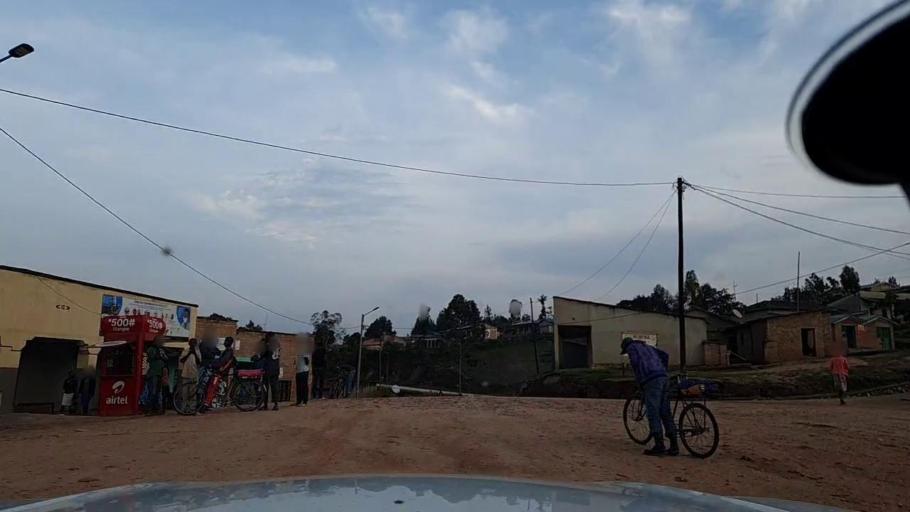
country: RW
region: Southern Province
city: Nyanza
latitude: -2.2220
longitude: 29.6480
